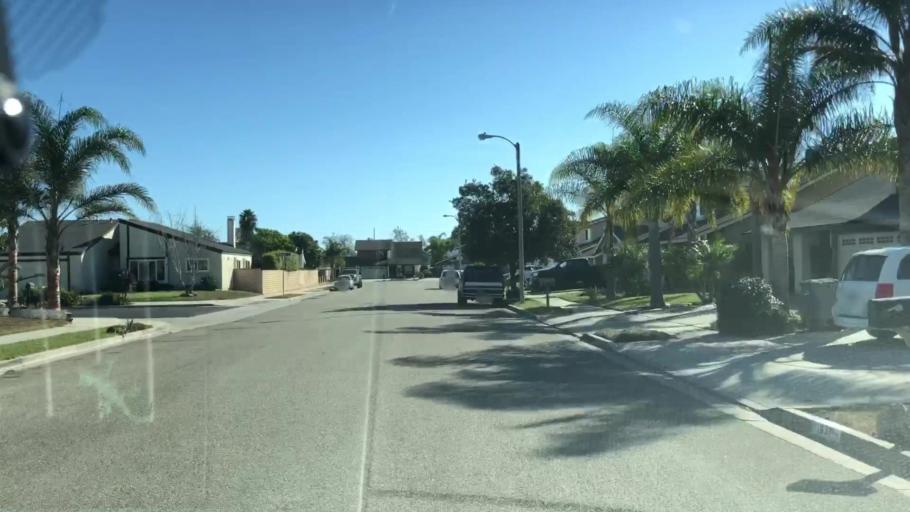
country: US
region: California
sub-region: Ventura County
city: Channel Islands Beach
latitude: 34.1843
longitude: -119.2115
